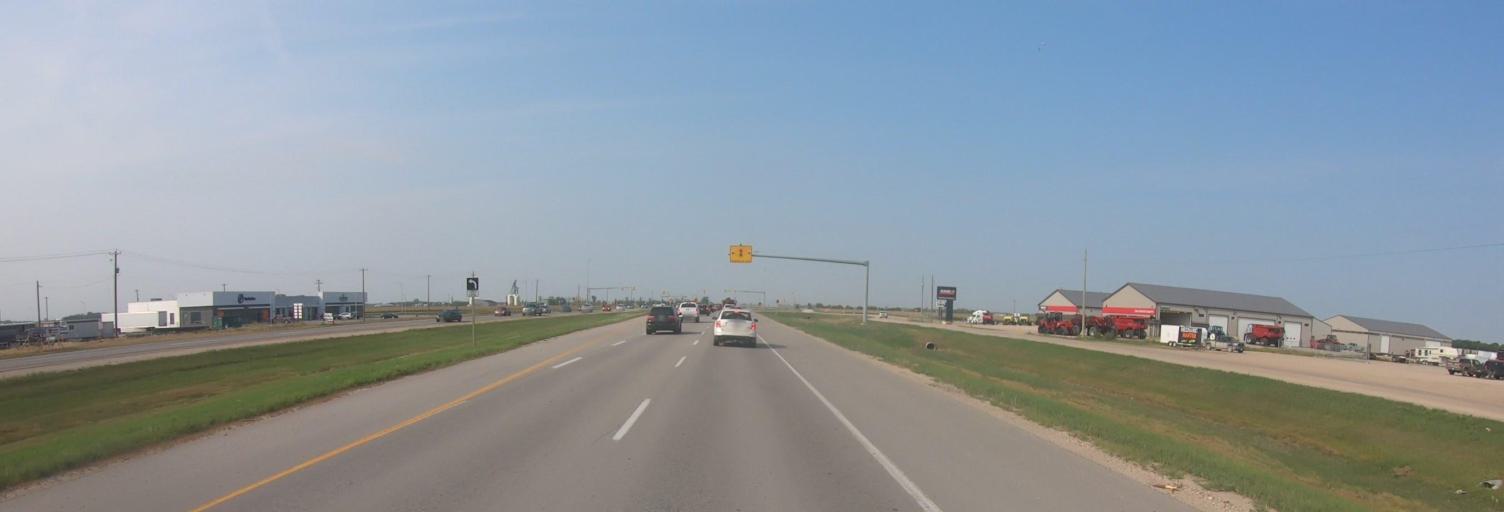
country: CA
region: Manitoba
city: Steinbach
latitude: 49.5650
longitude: -96.6878
